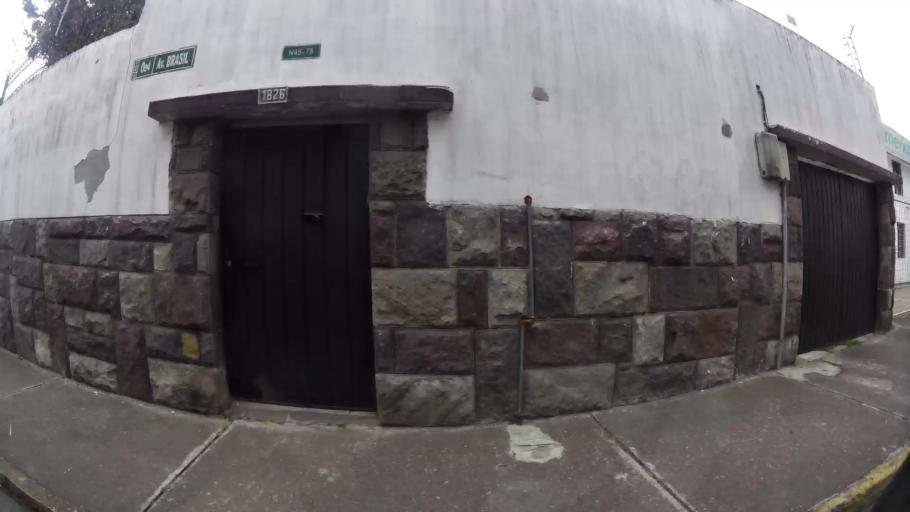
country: EC
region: Pichincha
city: Quito
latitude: -0.1585
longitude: -78.4904
